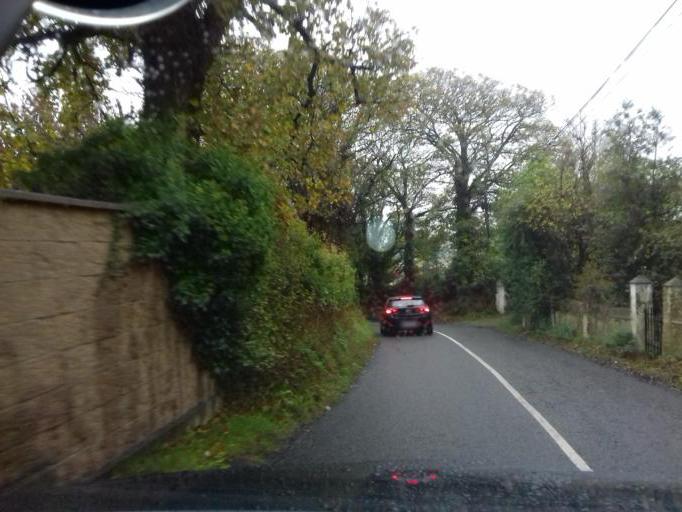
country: IE
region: Leinster
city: Ballyboden
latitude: 53.2628
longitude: -6.3108
